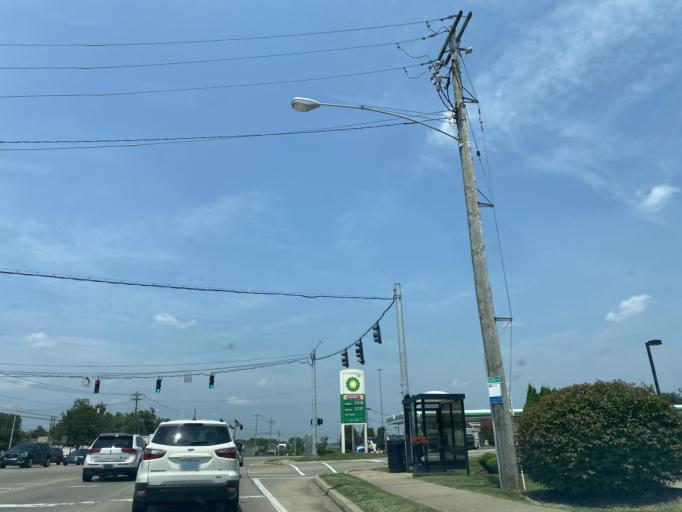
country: US
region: Kentucky
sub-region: Campbell County
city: Highland Heights
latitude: 39.0349
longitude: -84.4538
